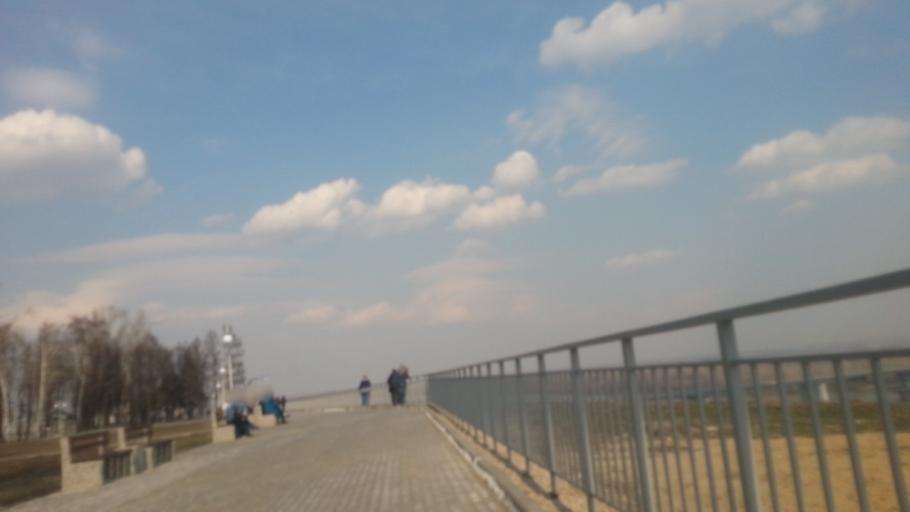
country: RU
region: Altai Krai
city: Zaton
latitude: 53.3211
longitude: 83.7943
